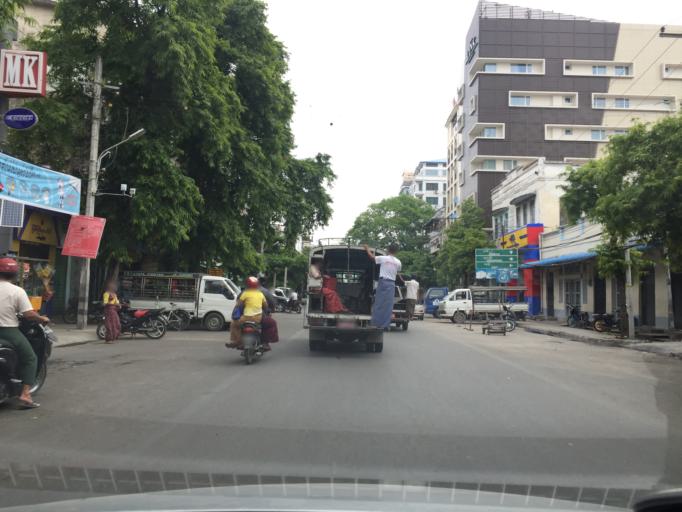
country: MM
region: Mandalay
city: Mandalay
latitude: 21.9809
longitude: 96.0793
